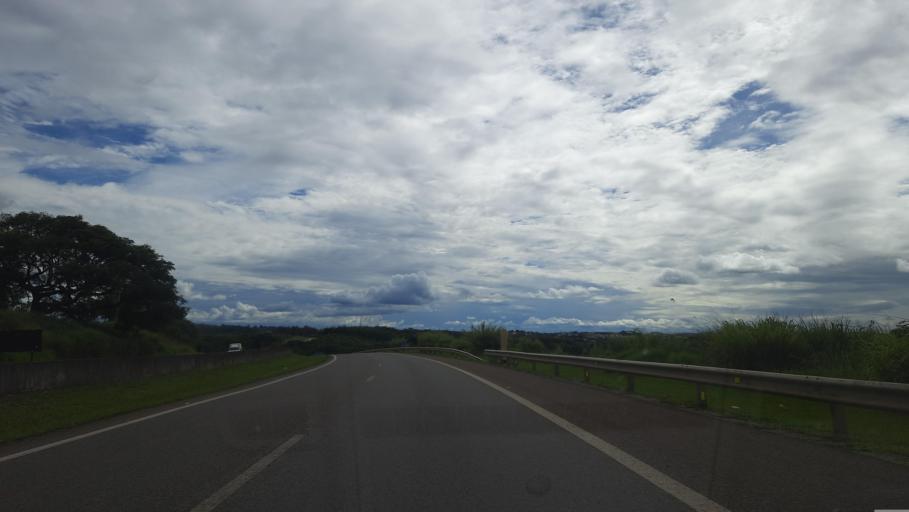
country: BR
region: Sao Paulo
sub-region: Sao Joao Da Boa Vista
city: Sao Joao da Boa Vista
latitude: -21.9535
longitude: -46.7293
